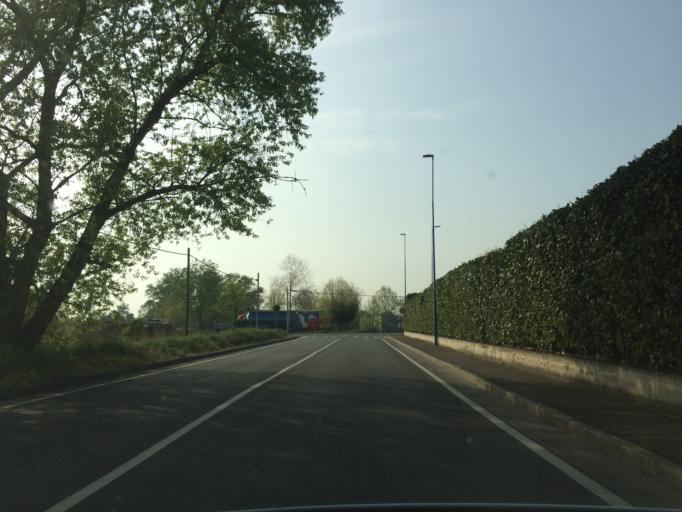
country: IT
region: Lombardy
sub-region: Provincia di Brescia
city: Folzano
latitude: 45.5134
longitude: 10.2042
